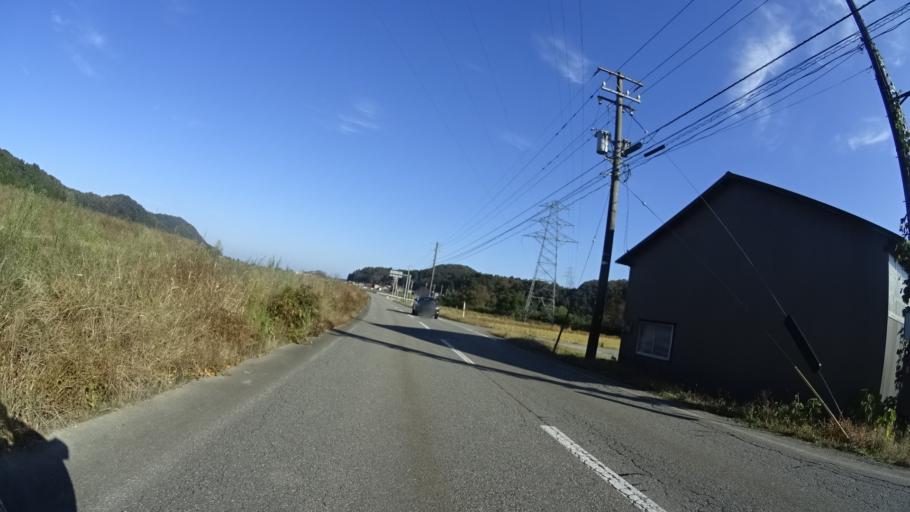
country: JP
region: Ishikawa
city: Komatsu
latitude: 36.2643
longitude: 136.3936
